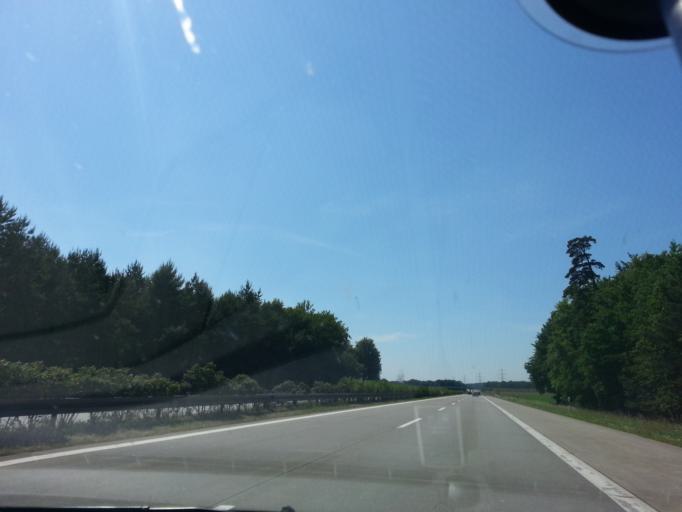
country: DE
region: Mecklenburg-Vorpommern
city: Zarrentin
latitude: 53.5113
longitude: 10.9612
